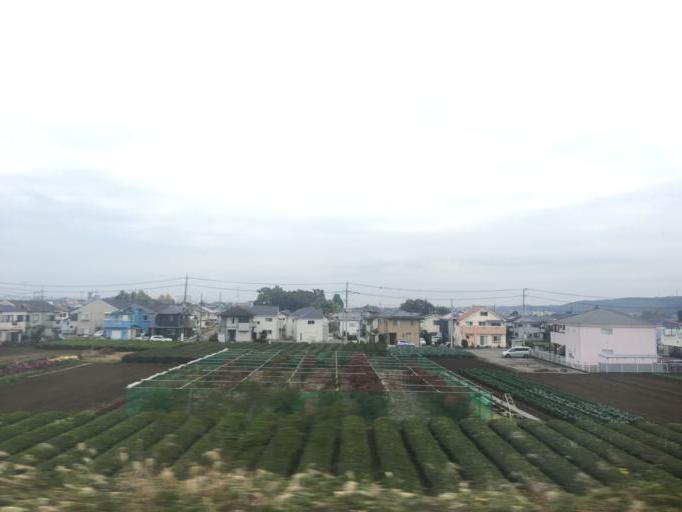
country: JP
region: Saitama
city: Hanno
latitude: 35.8416
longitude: 139.3340
